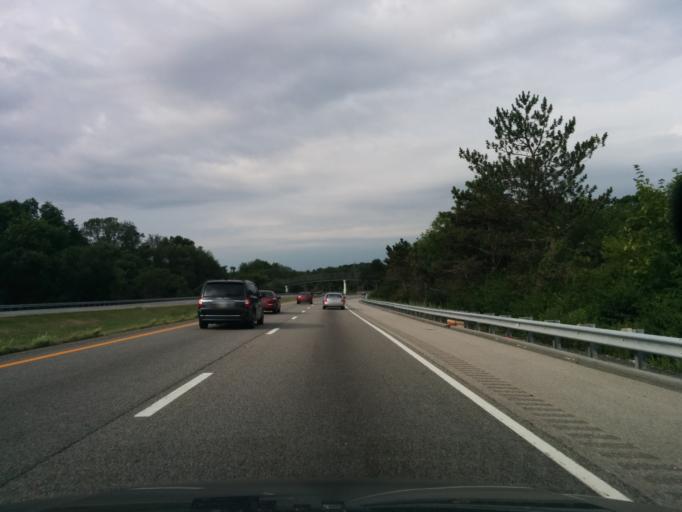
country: US
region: Delaware
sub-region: New Castle County
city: Claymont
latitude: 39.8068
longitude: -75.4641
